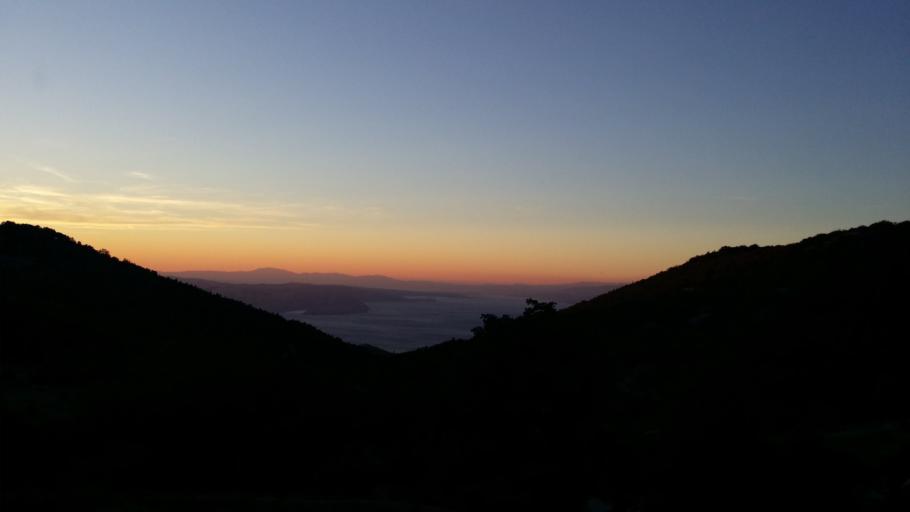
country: HR
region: Licko-Senjska
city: Senj
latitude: 44.8829
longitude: 14.9718
